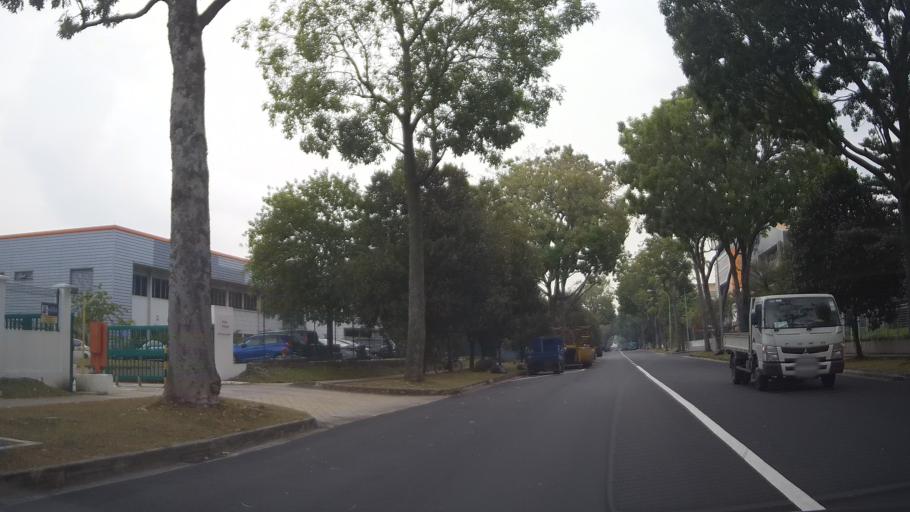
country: MY
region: Johor
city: Johor Bahru
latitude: 1.3154
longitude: 103.6758
